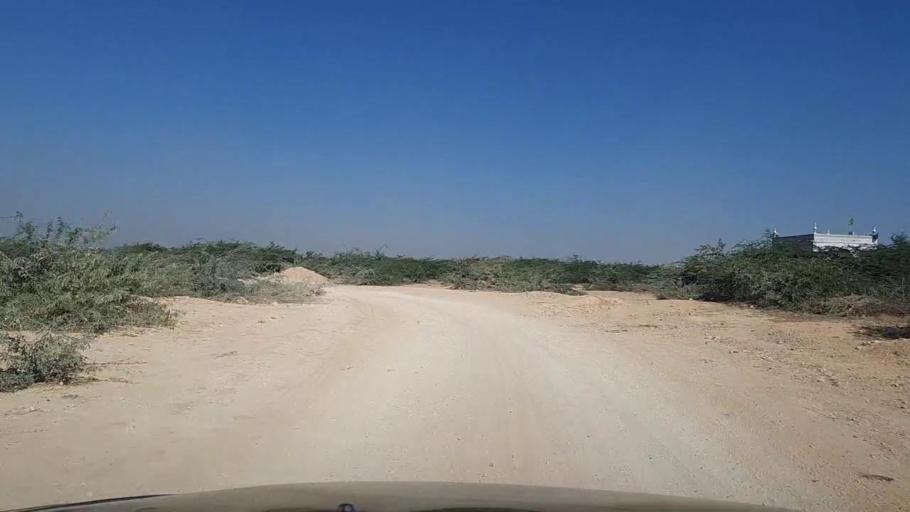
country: PK
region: Sindh
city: Thatta
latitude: 24.6217
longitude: 67.8394
